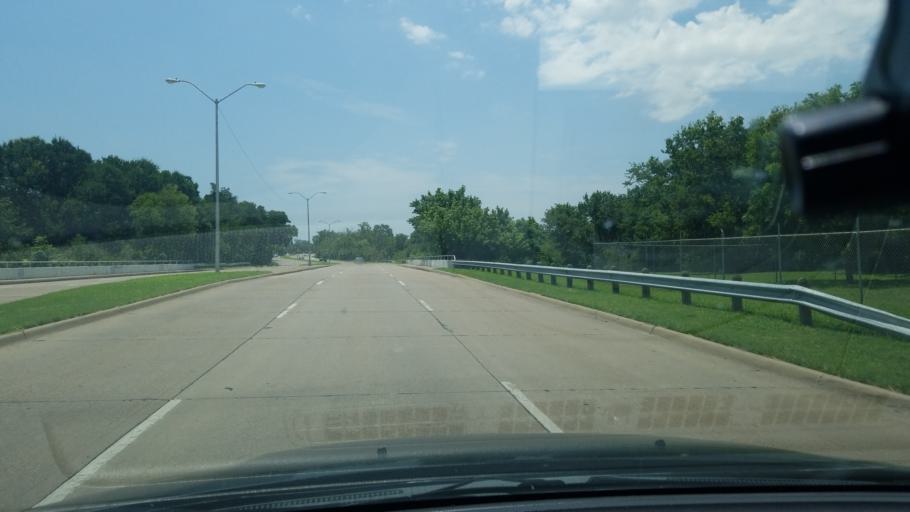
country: US
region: Texas
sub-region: Dallas County
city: Balch Springs
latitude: 32.7250
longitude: -96.6662
